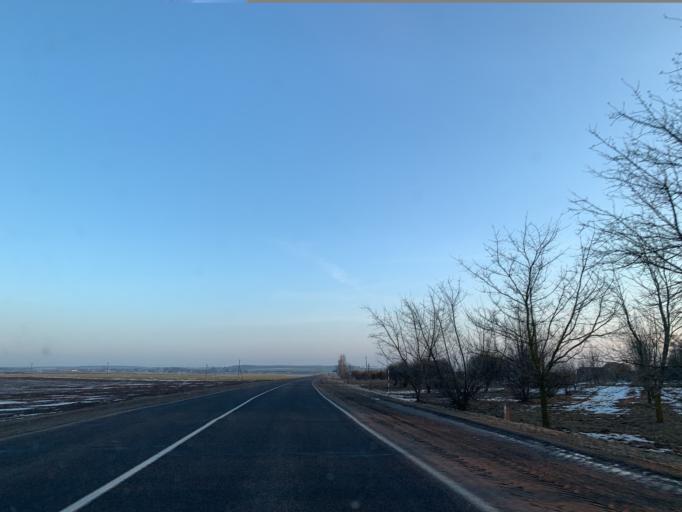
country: BY
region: Minsk
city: Haradzyeya
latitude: 53.3190
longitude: 26.5593
